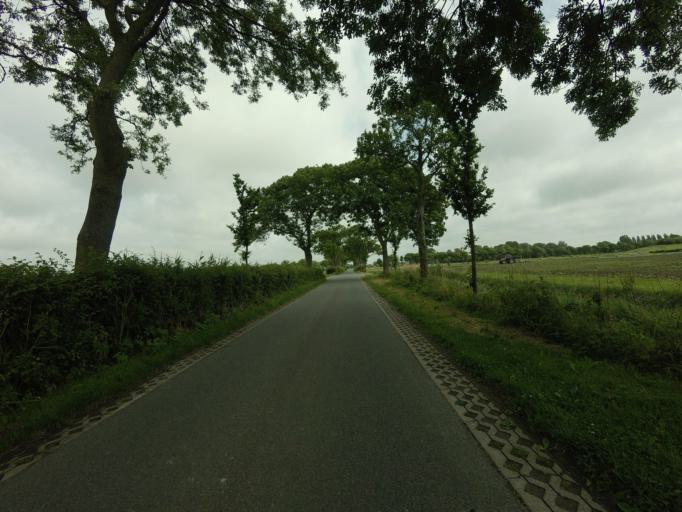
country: NL
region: North Holland
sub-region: Gemeente Schagen
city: Harenkarspel
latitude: 52.7327
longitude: 4.7339
